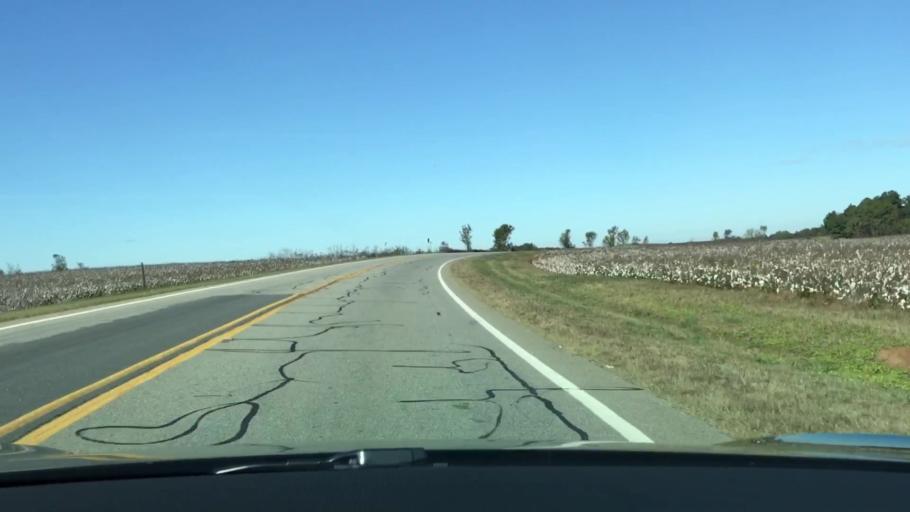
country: US
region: Georgia
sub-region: Warren County
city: Warrenton
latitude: 33.3558
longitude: -82.5926
